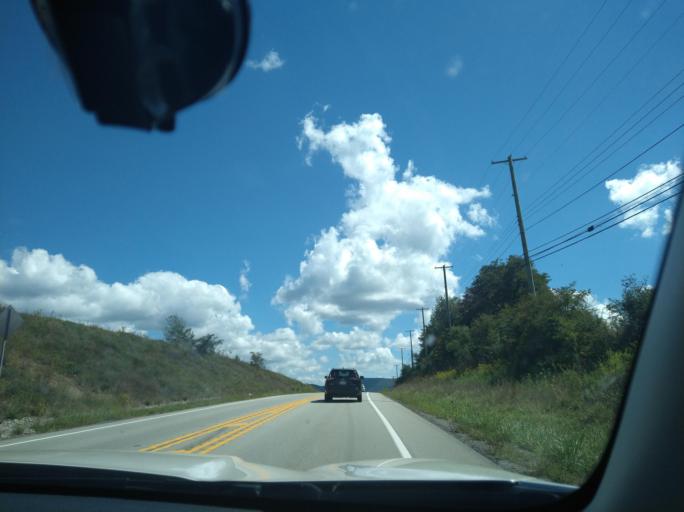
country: US
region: Pennsylvania
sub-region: Fayette County
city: Bear Rocks
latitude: 40.1027
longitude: -79.3682
